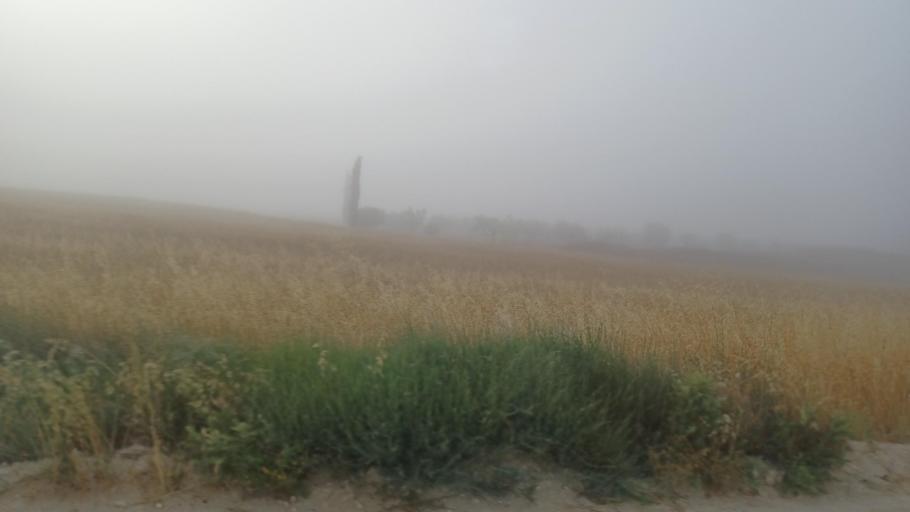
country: CY
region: Ammochostos
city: Acheritou
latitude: 35.0896
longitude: 33.8761
